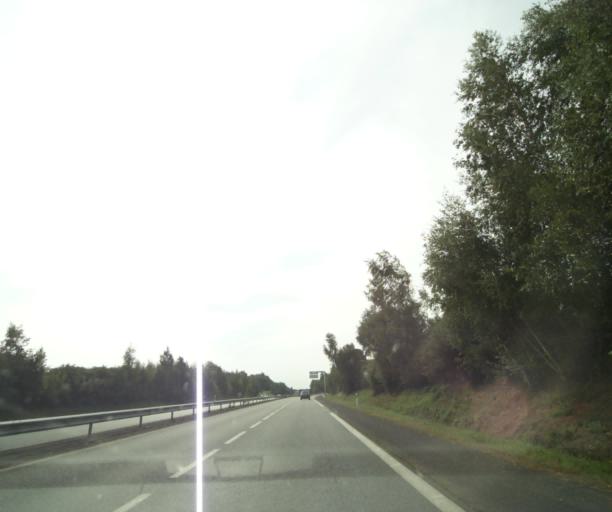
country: FR
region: Brittany
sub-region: Departement d'Ille-et-Vilaine
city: Plerguer
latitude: 48.5454
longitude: -1.8547
